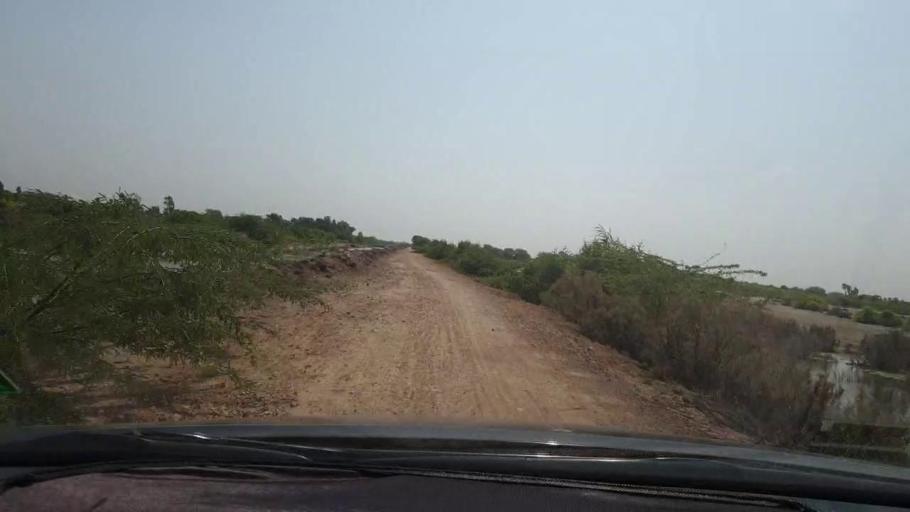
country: PK
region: Sindh
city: Tando Bago
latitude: 24.7967
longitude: 69.1068
